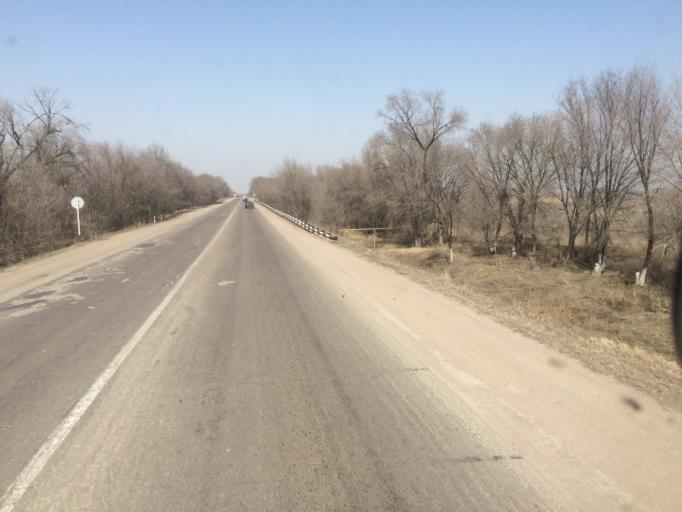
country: KZ
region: Almaty Oblysy
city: Burunday
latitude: 43.3118
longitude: 76.6657
